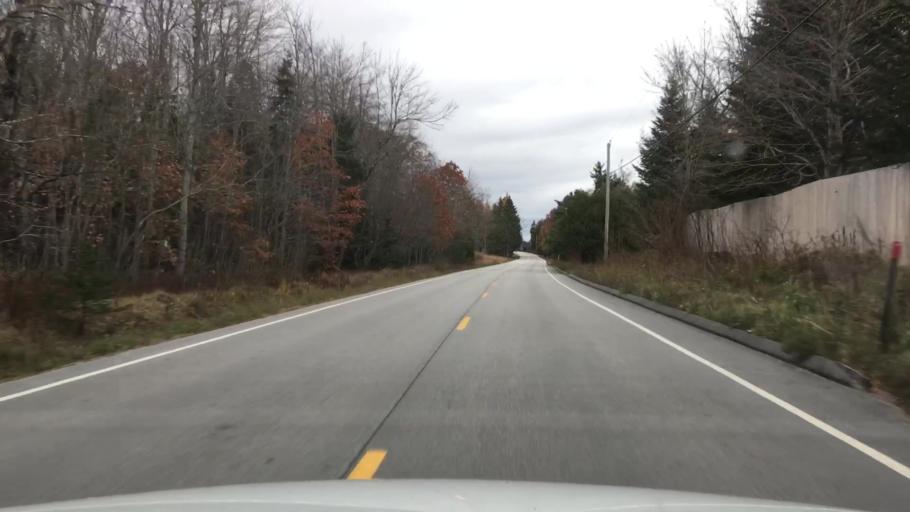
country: US
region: Maine
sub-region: Hancock County
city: Penobscot
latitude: 44.4732
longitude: -68.6371
